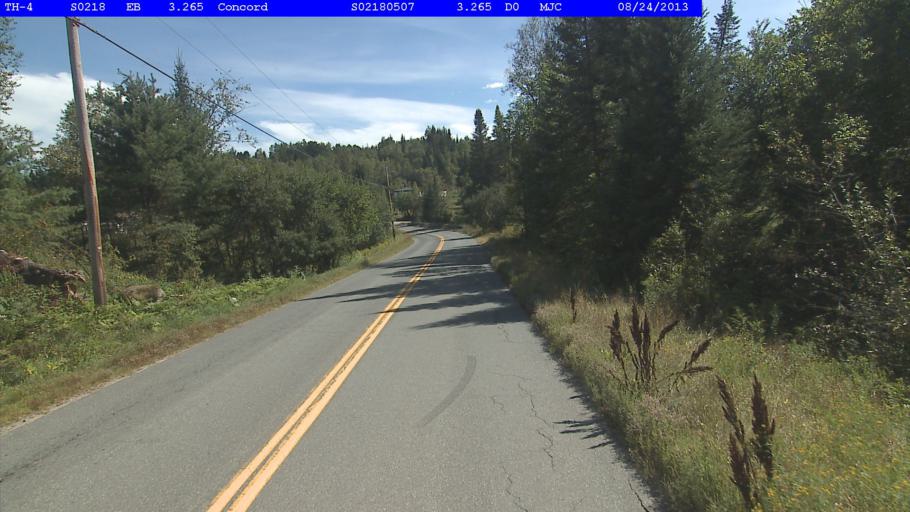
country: US
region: New Hampshire
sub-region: Grafton County
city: Littleton
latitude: 44.4231
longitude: -71.7518
